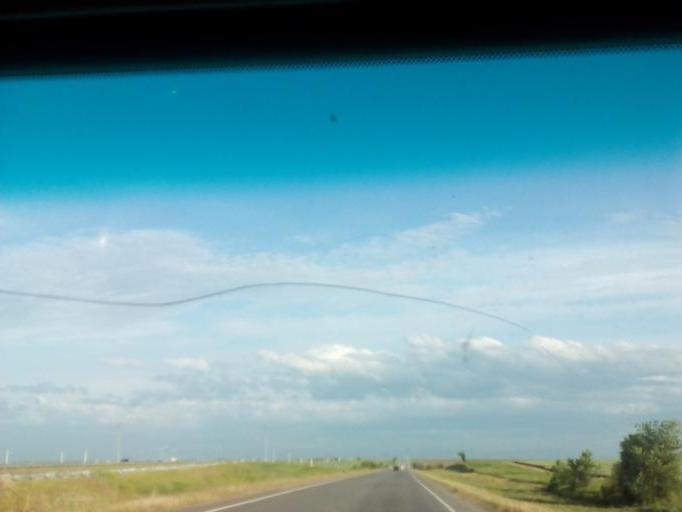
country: KZ
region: Ongtustik Qazaqstan
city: Temirlanovka
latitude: 42.5338
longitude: 69.3364
